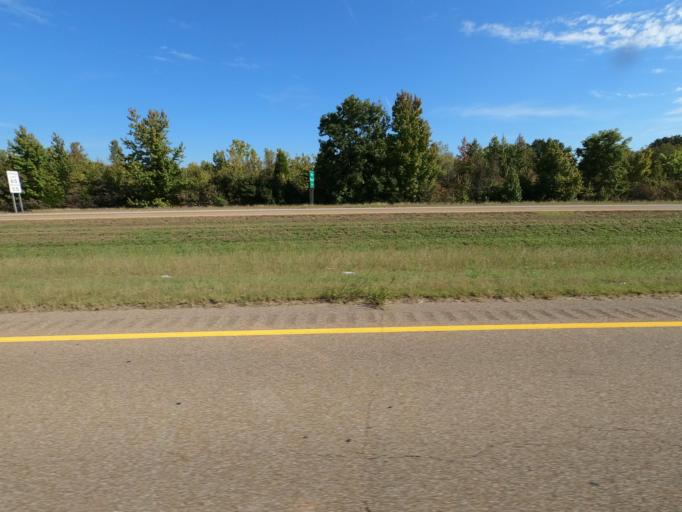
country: US
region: Tennessee
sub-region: Shelby County
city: Millington
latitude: 35.3240
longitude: -89.8818
